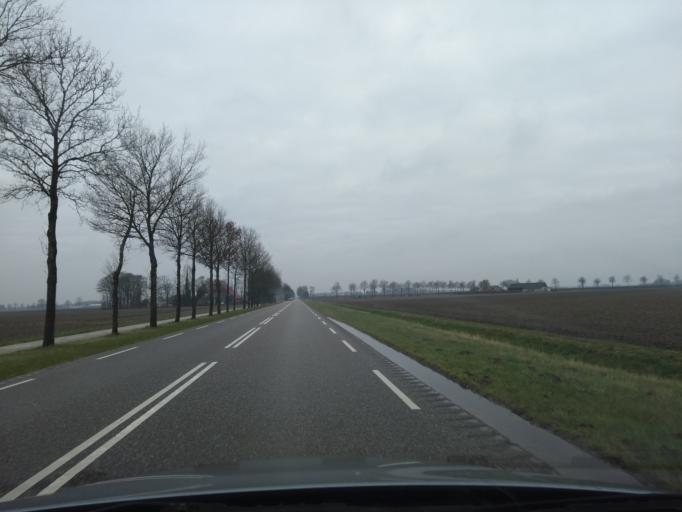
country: NL
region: Overijssel
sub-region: Gemeente Steenwijkerland
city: Vollenhove
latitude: 52.7029
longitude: 5.8956
